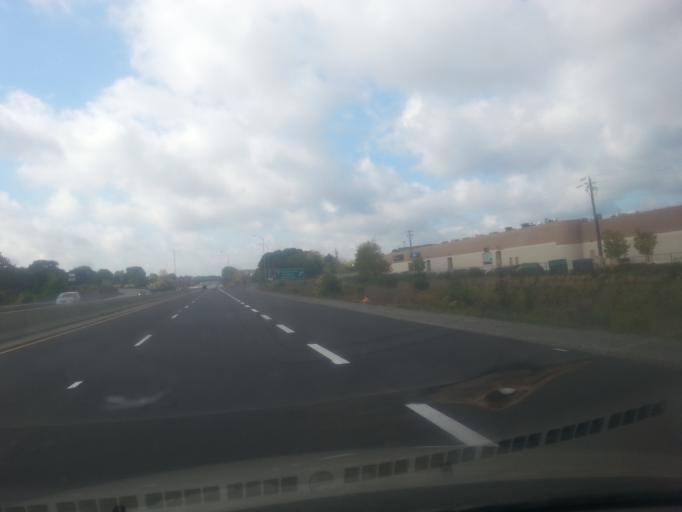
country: CA
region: Ontario
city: Brockville
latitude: 44.6026
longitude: -75.6972
